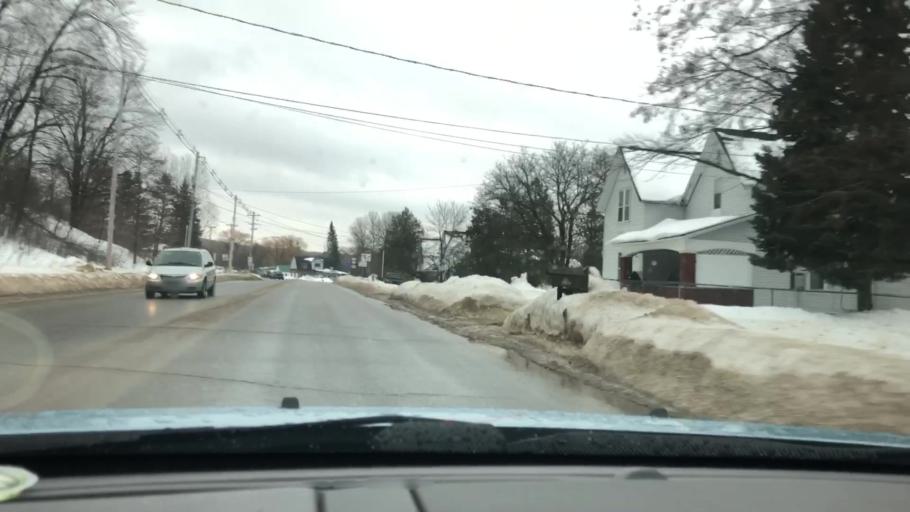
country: US
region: Michigan
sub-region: Charlevoix County
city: East Jordan
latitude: 45.1529
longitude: -85.1210
